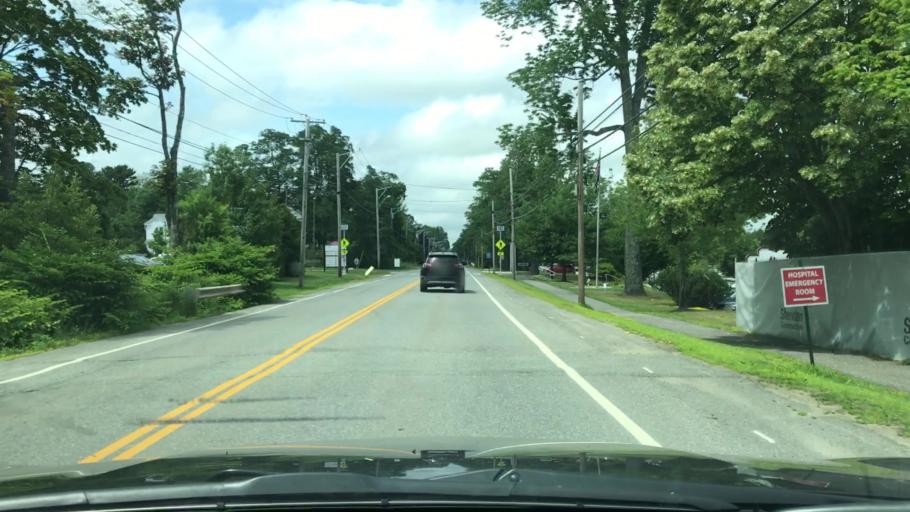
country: US
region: Maine
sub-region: Waldo County
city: Belfast
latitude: 44.4120
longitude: -68.9946
